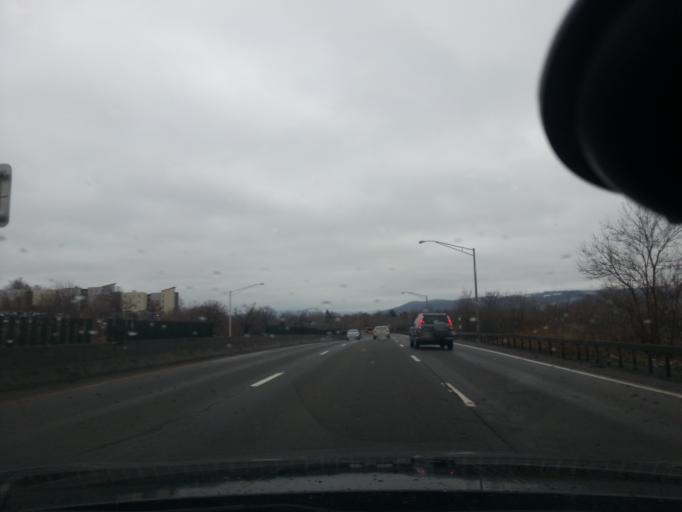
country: US
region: New York
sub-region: Onondaga County
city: Syracuse
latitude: 43.0370
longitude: -76.1424
